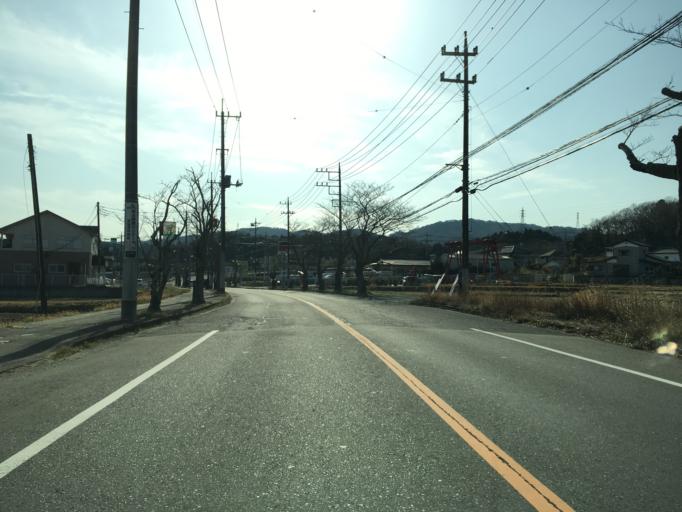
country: JP
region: Ibaraki
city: Takahagi
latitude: 36.7433
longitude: 140.6902
